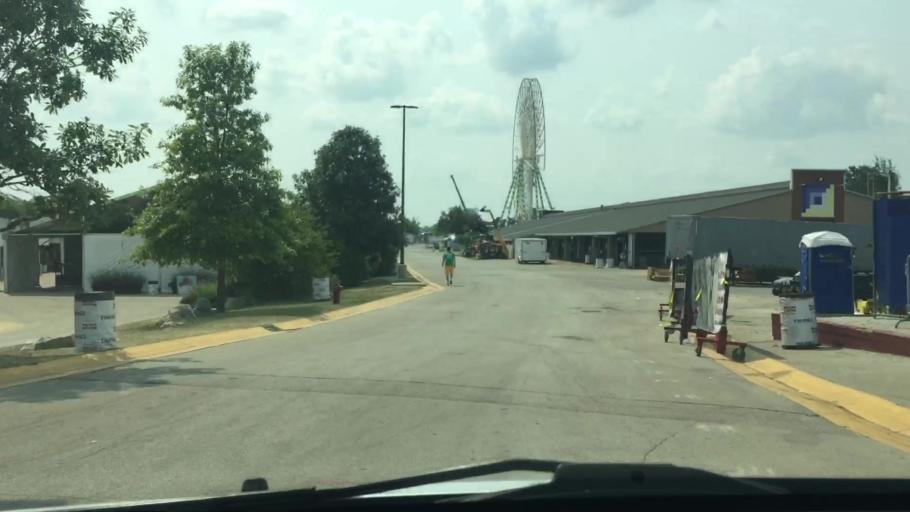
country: US
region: Wisconsin
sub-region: Milwaukee County
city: West Allis
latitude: 43.0237
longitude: -88.0165
